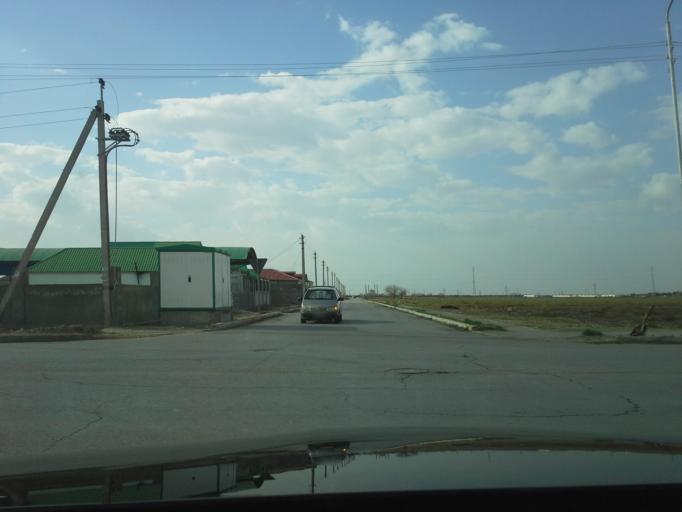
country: TM
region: Ahal
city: Ashgabat
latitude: 37.9923
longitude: 58.2912
